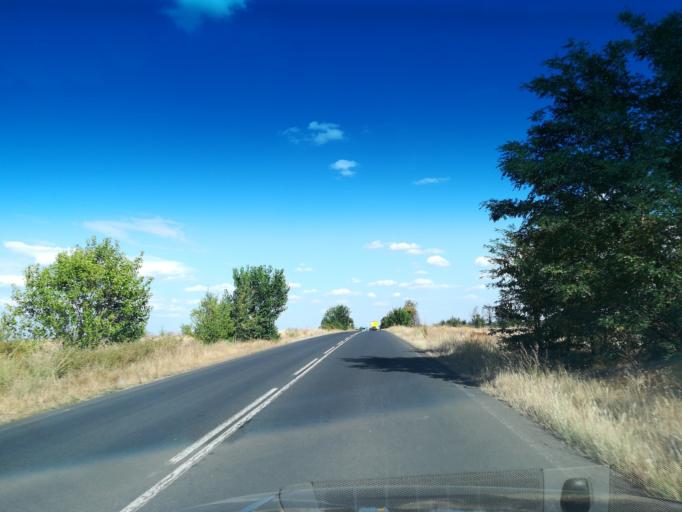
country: BG
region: Stara Zagora
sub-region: Obshtina Chirpan
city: Chirpan
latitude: 42.0582
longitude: 25.2862
